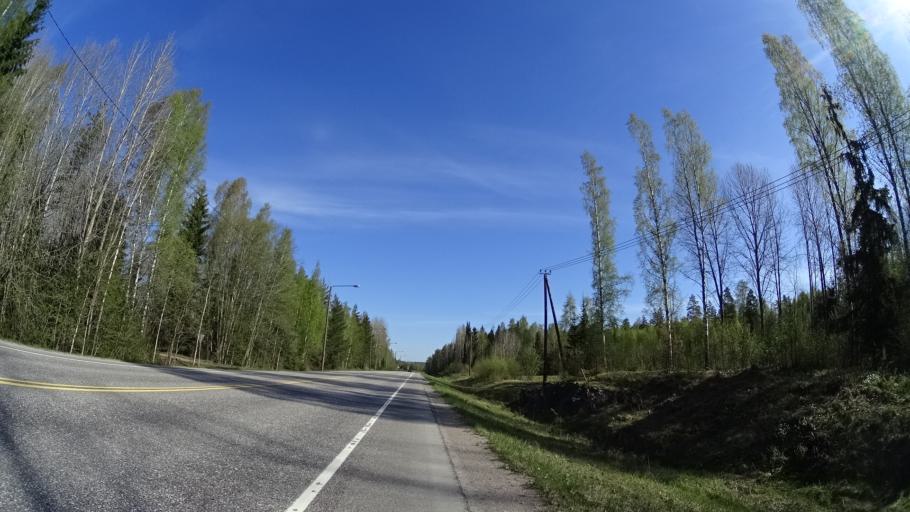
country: FI
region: Uusimaa
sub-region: Helsinki
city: Nurmijaervi
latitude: 60.3837
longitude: 24.8076
